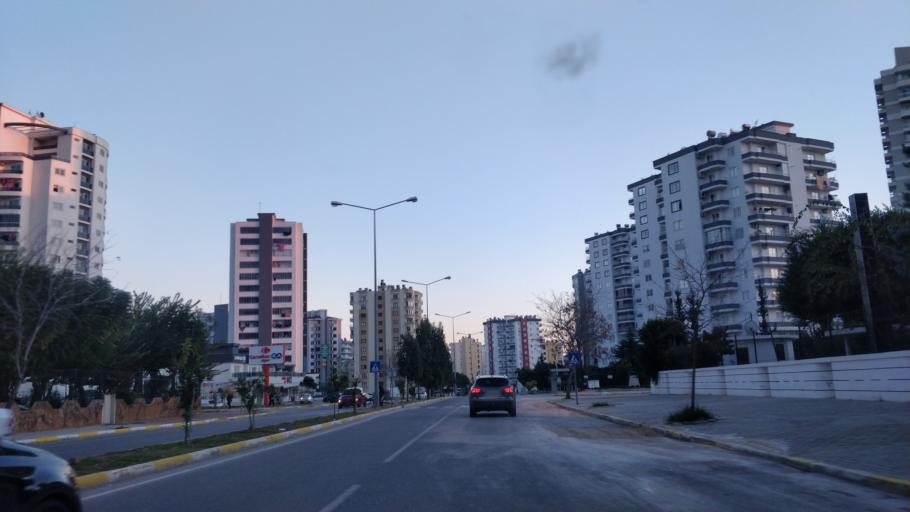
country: TR
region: Mersin
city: Mercin
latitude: 36.7950
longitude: 34.5870
